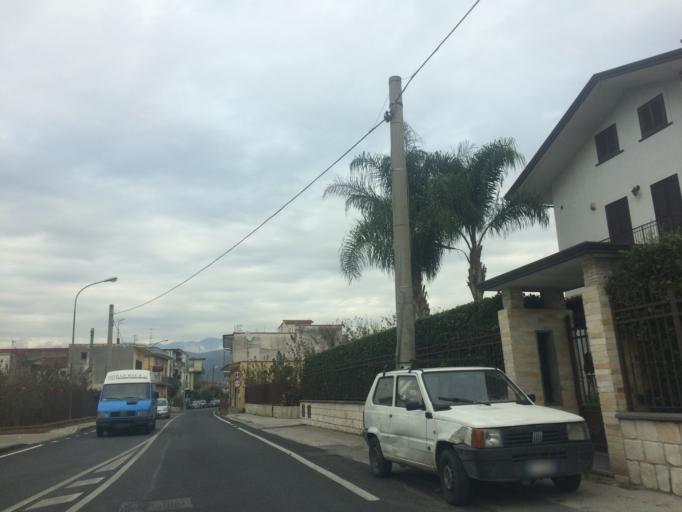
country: IT
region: Campania
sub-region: Provincia di Napoli
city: Piazzolla
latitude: 40.8971
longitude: 14.5219
